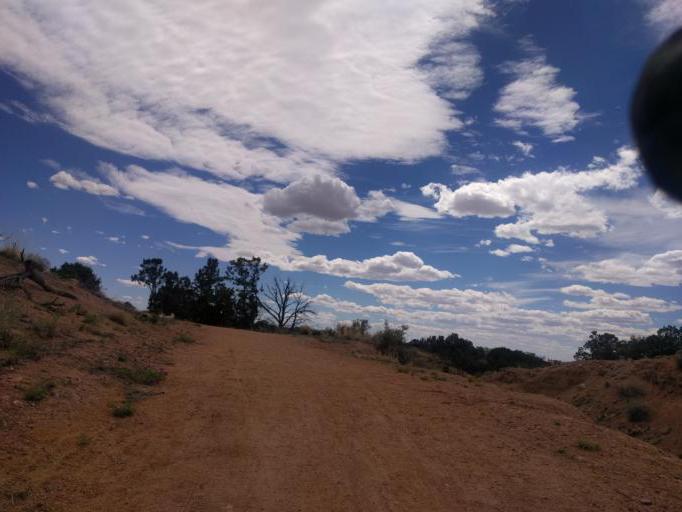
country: US
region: New Mexico
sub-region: Santa Fe County
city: Agua Fria
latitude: 35.6200
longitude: -105.9618
